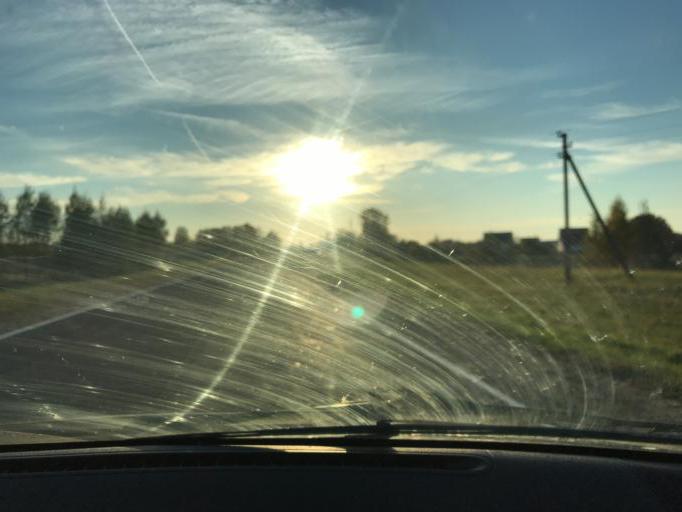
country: BY
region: Brest
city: Horad Kobryn
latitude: 52.2196
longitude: 24.4208
